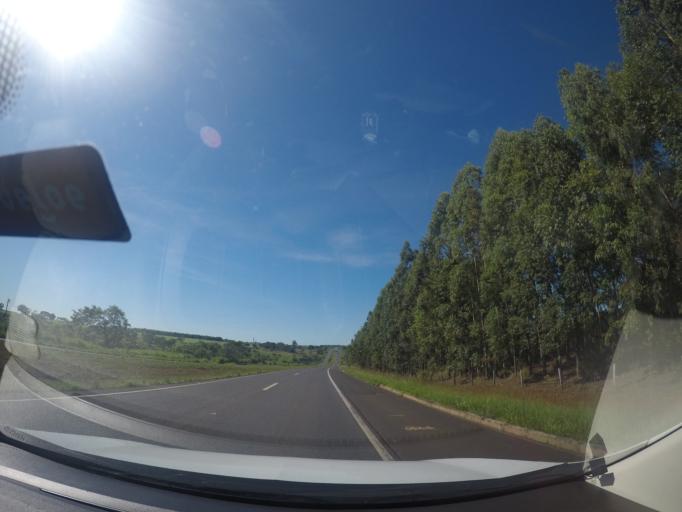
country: BR
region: Goias
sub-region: Morrinhos
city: Morrinhos
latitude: -17.6848
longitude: -49.1596
